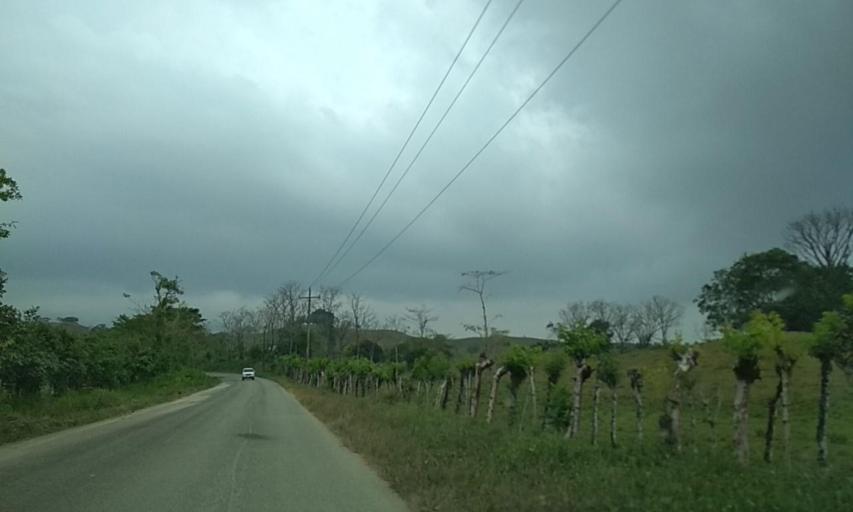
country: MX
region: Tabasco
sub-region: Huimanguillo
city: Francisco Rueda
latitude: 17.6071
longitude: -94.0925
